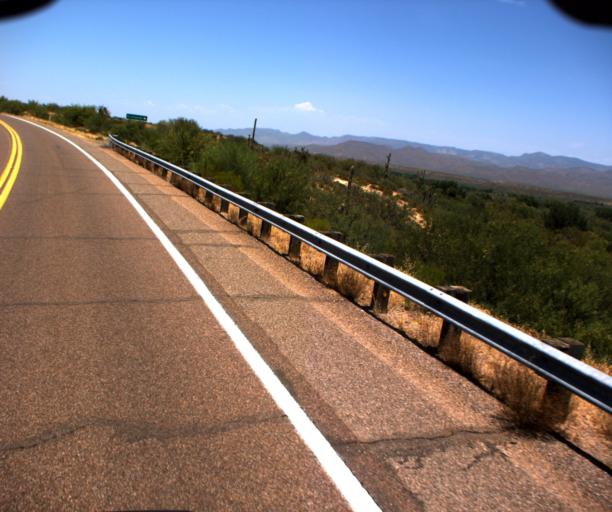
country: US
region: Arizona
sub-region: Gila County
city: Tonto Basin
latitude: 33.7857
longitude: -111.2636
